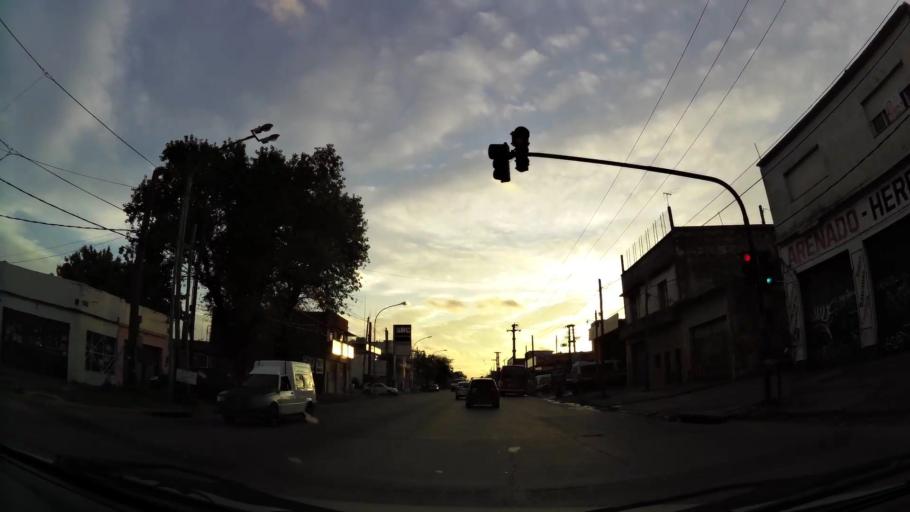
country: AR
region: Buenos Aires
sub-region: Partido de Lomas de Zamora
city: Lomas de Zamora
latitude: -34.7666
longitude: -58.3718
